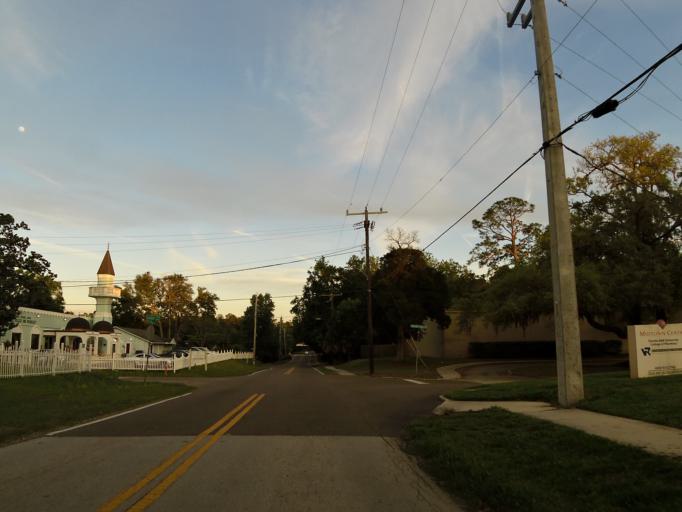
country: US
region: Florida
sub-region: Duval County
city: Jacksonville
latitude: 30.3019
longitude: -81.6149
